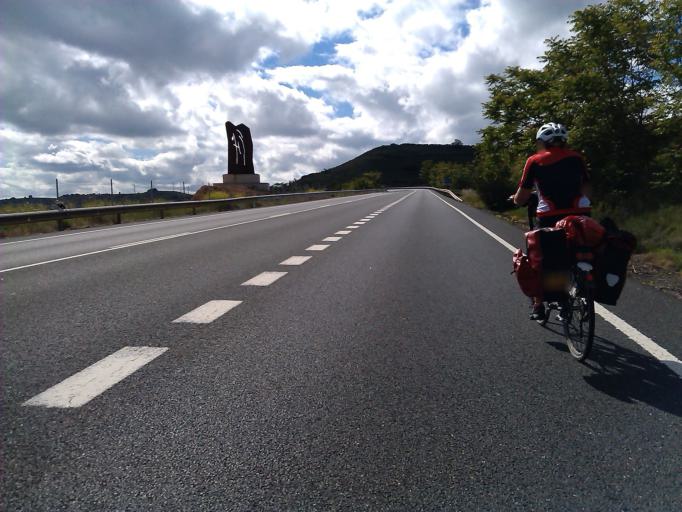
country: ES
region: La Rioja
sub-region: Provincia de La Rioja
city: Torrecilla sobre Alesanco
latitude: 42.4385
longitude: -2.8468
